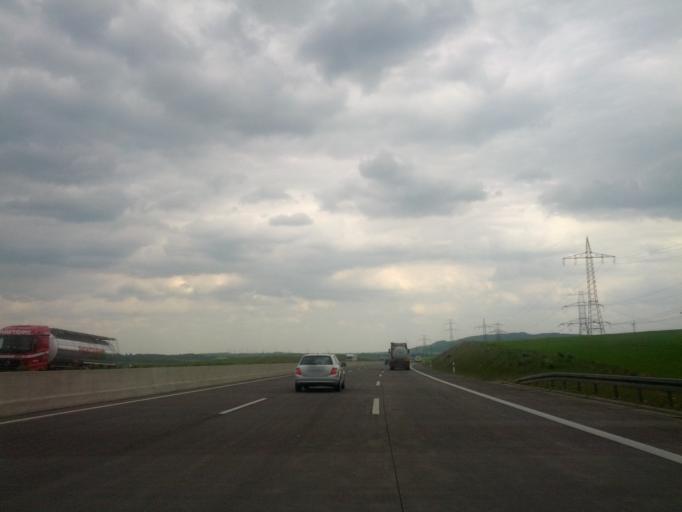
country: DE
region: Thuringia
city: Bischofroda
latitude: 51.0123
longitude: 10.3836
